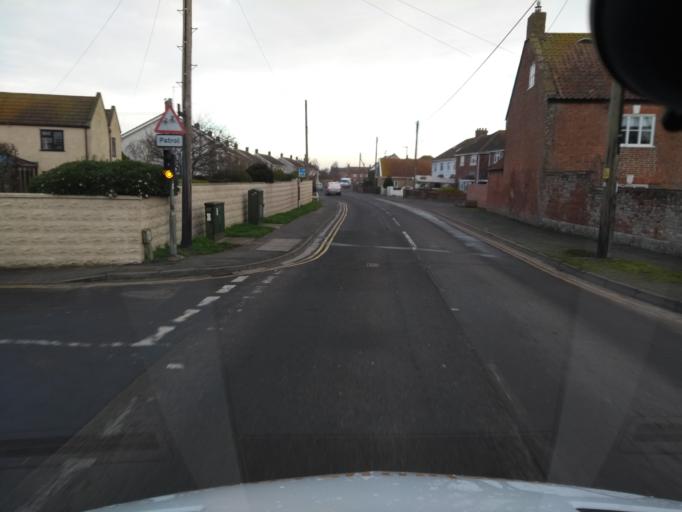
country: GB
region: England
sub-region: Somerset
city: Burnham-on-Sea
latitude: 51.2614
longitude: -3.0073
